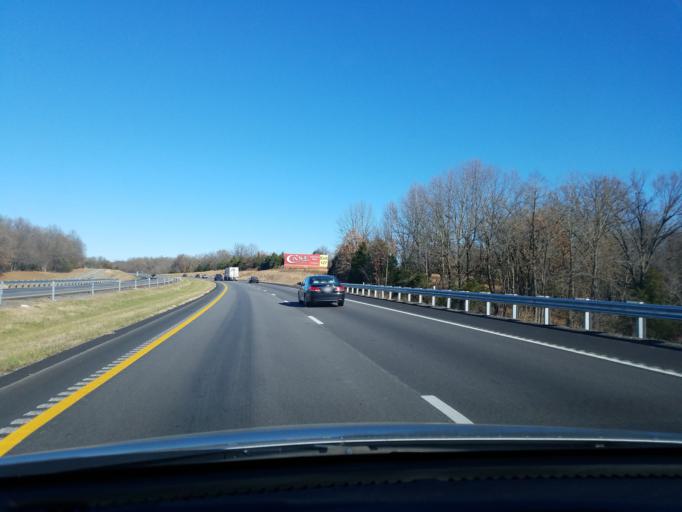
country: US
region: Missouri
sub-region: Webster County
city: Marshfield
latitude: 37.3578
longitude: -92.9119
